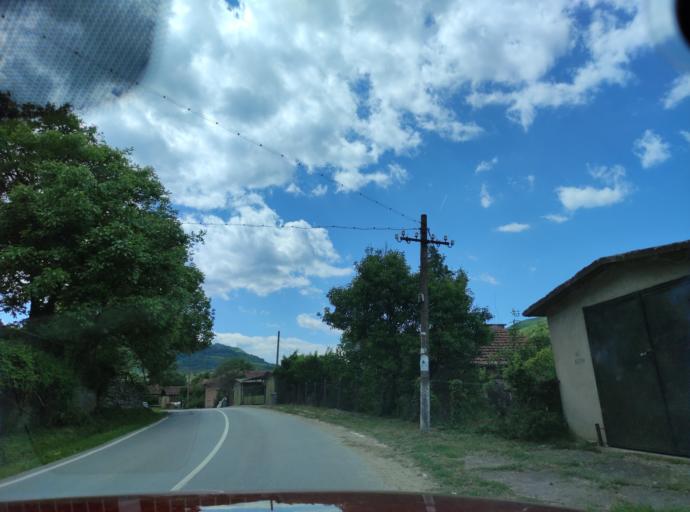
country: BG
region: Montana
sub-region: Obshtina Chiprovtsi
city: Chiprovtsi
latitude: 43.4690
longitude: 22.8608
